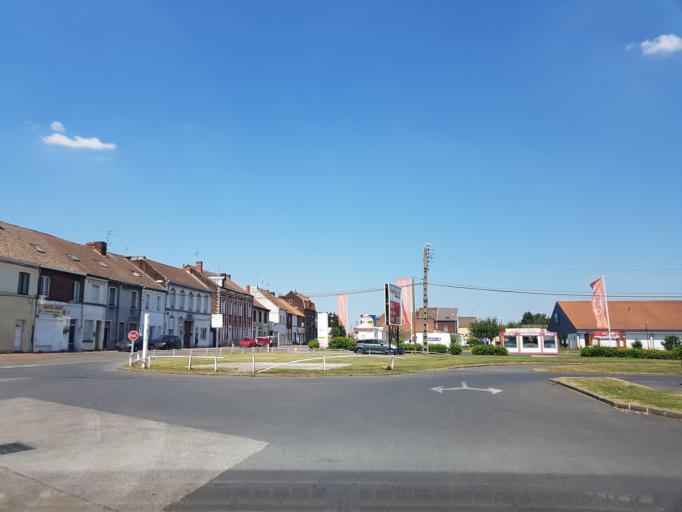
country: FR
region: Nord-Pas-de-Calais
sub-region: Departement du Nord
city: Lourches
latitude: 50.3111
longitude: 3.3460
